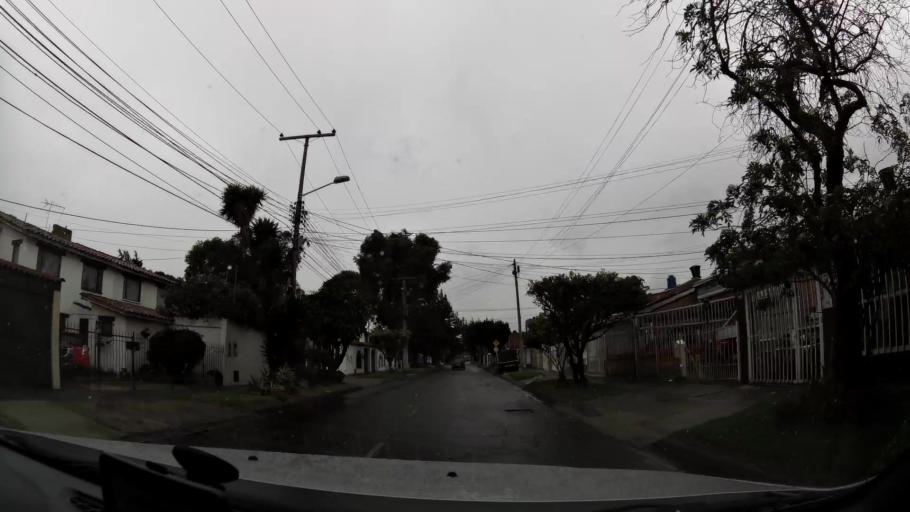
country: CO
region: Bogota D.C.
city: Bogota
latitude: 4.6621
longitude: -74.1255
